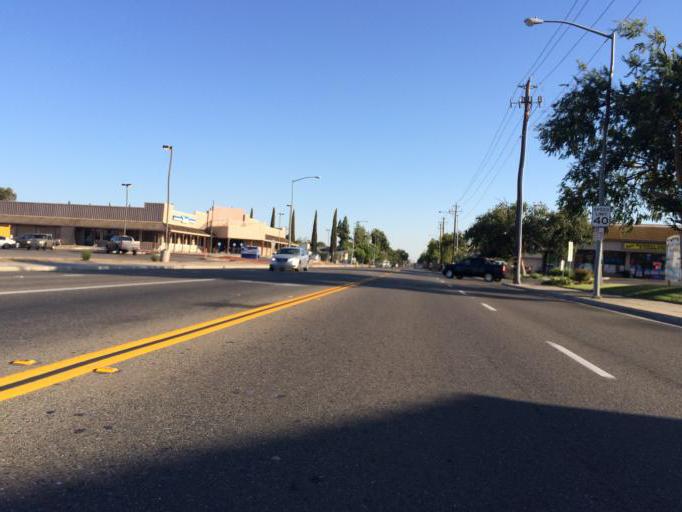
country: US
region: California
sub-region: Fresno County
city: Clovis
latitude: 36.8227
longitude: -119.7090
